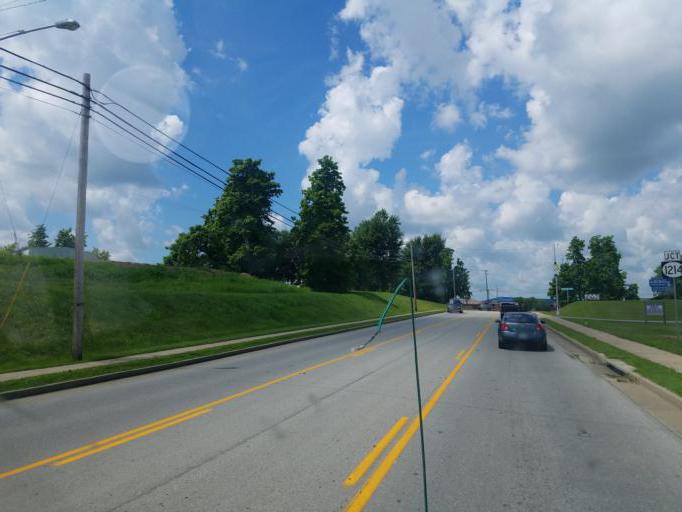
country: US
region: Kentucky
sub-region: Grayson County
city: Leitchfield
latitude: 37.4846
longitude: -86.2782
